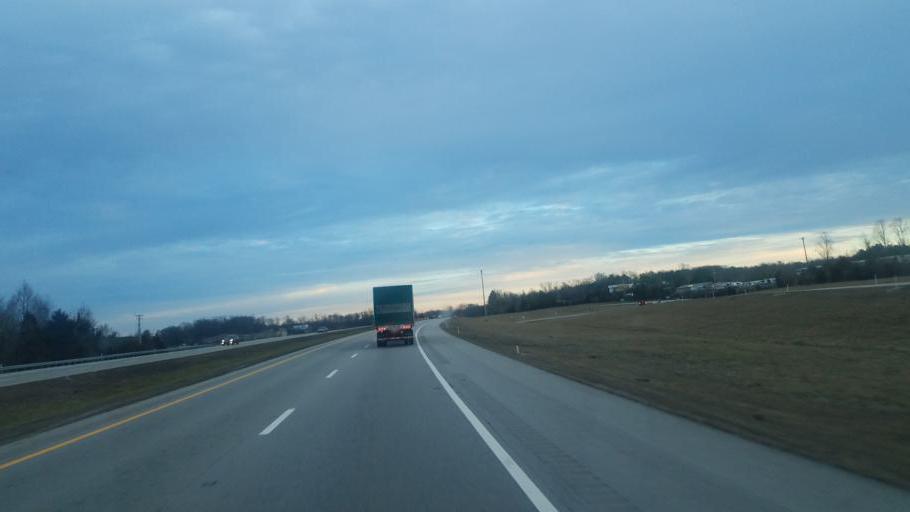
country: US
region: Tennessee
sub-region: Putnam County
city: Cookeville
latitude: 36.0997
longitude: -85.5048
